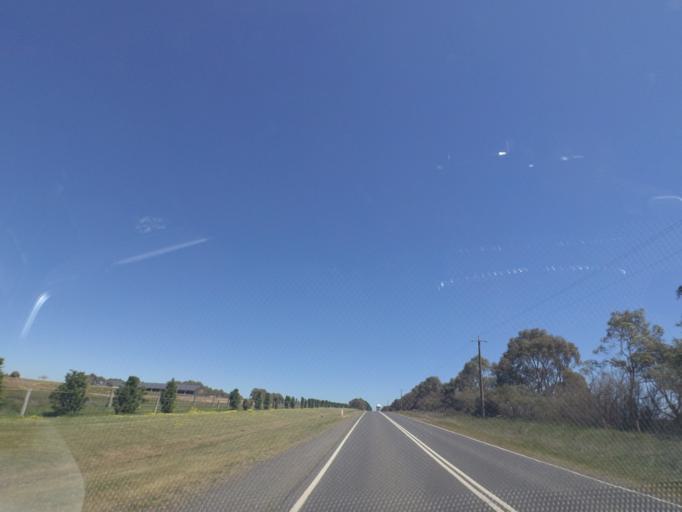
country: AU
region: Victoria
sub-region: Hume
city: Sunbury
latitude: -37.2850
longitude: 144.7710
